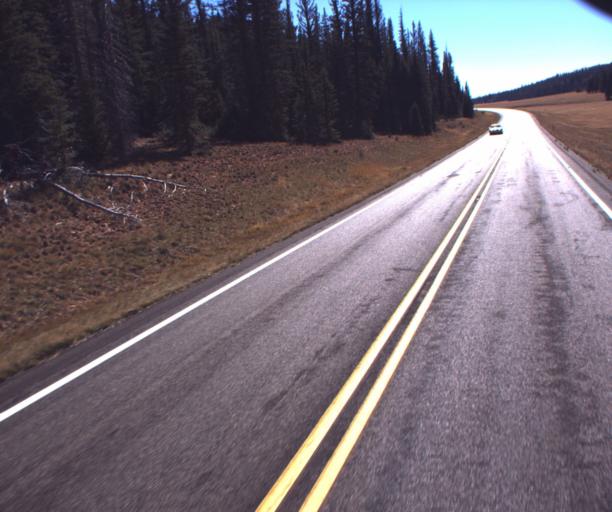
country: US
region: Arizona
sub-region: Coconino County
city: Grand Canyon
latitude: 36.3800
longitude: -112.1260
